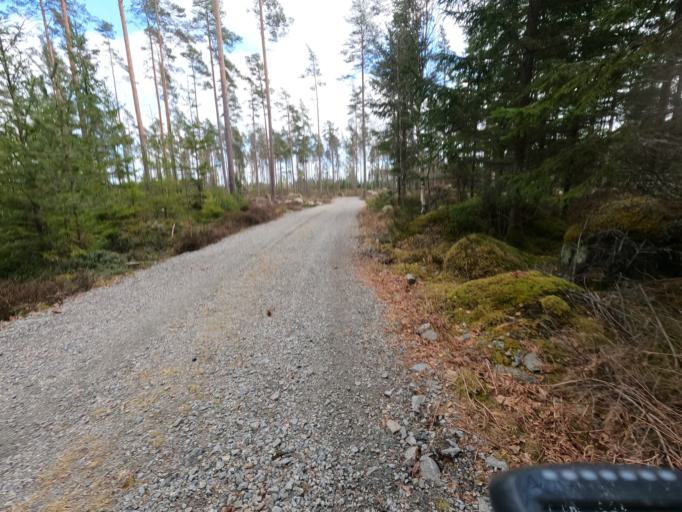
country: SE
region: Kronoberg
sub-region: Alvesta Kommun
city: Vislanda
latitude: 56.8138
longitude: 14.3834
